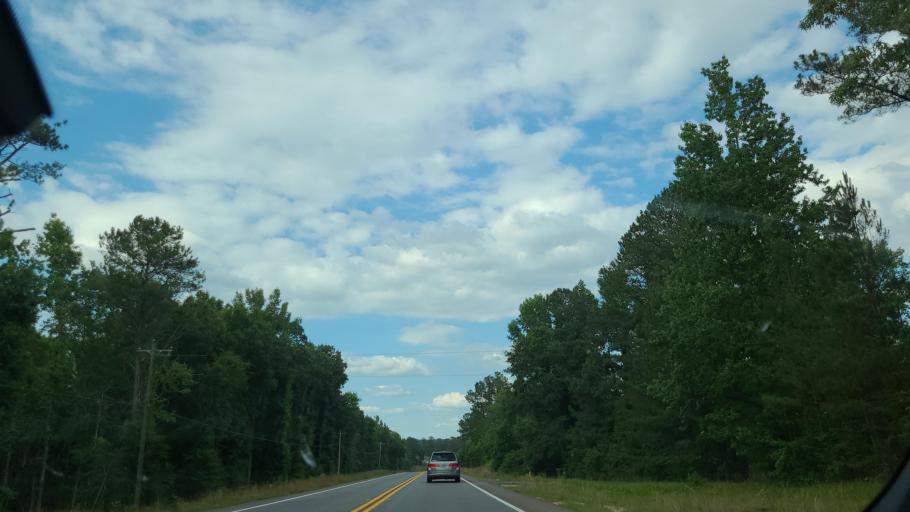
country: US
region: Georgia
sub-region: Putnam County
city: Eatonton
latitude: 33.2585
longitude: -83.4222
